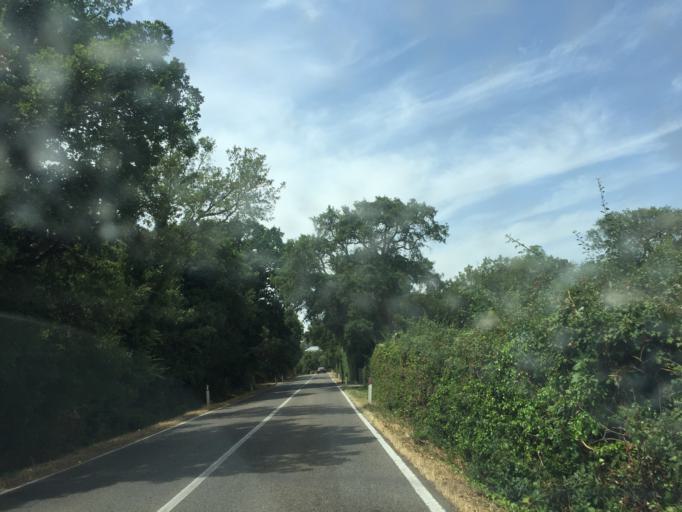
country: IT
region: Sardinia
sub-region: Provincia di Olbia-Tempio
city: Aggius
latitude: 40.9180
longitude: 9.0735
